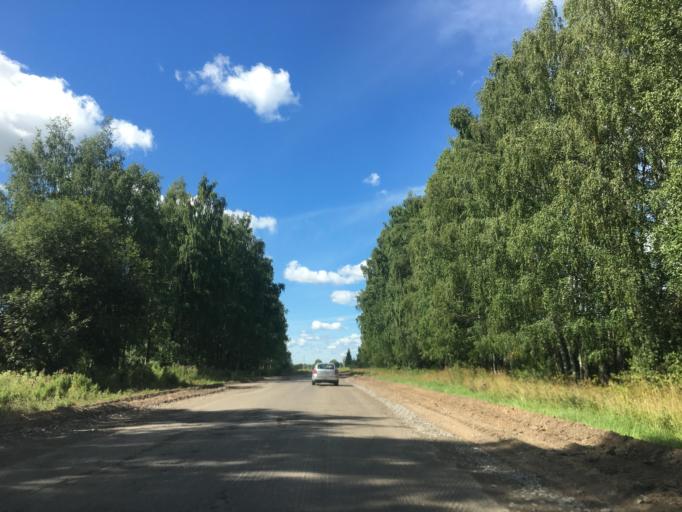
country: RU
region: Pskov
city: Palkino
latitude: 57.5522
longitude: 28.0529
